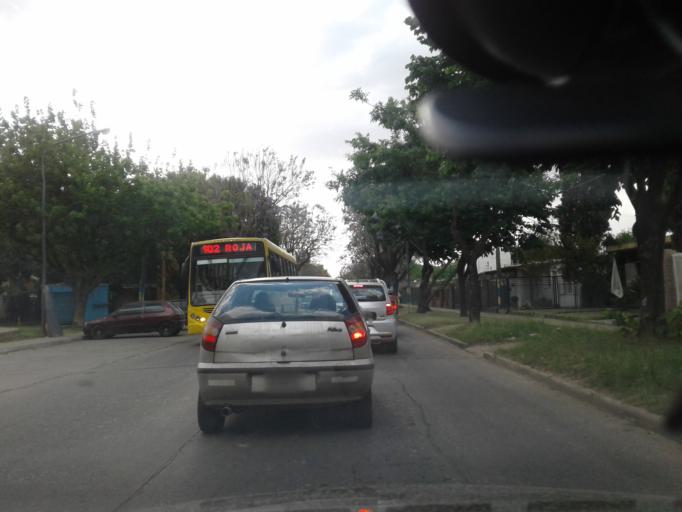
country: AR
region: Santa Fe
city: Granadero Baigorria
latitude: -32.8939
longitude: -60.7151
